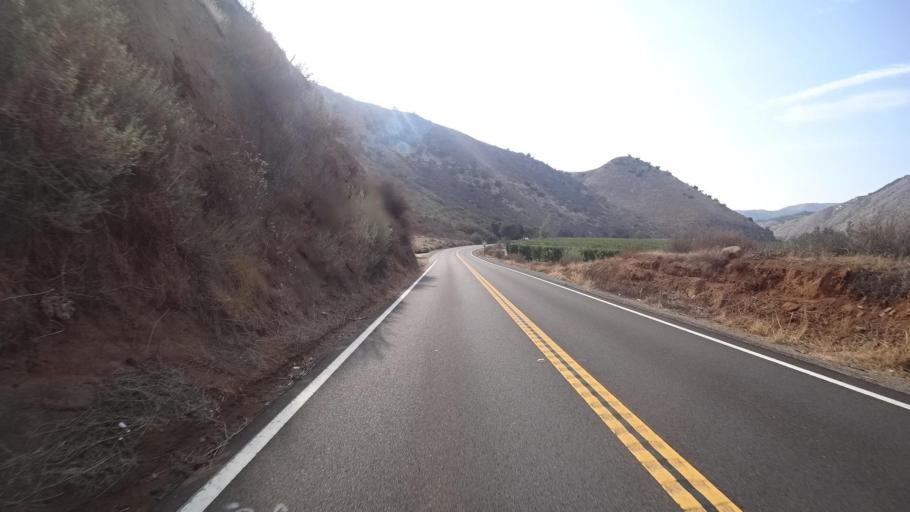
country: US
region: California
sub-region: San Diego County
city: San Pasqual
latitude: 33.0858
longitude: -116.9322
